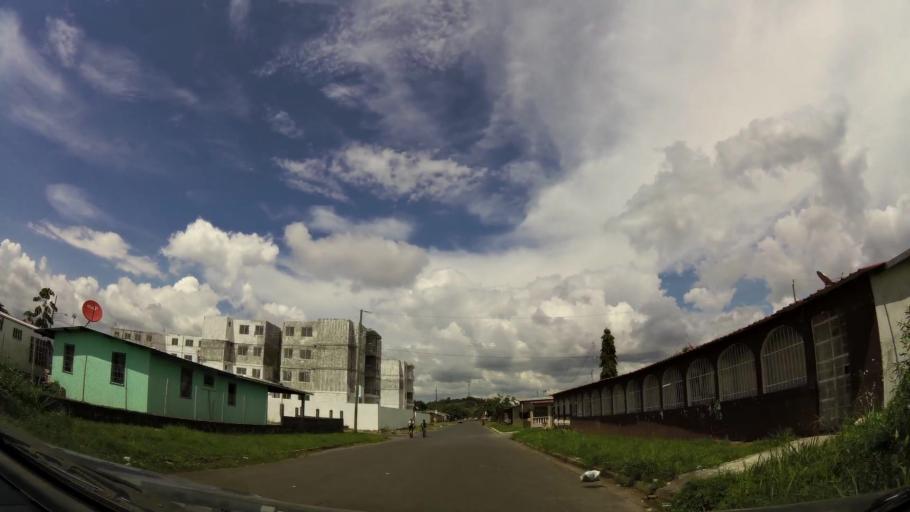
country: PA
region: Panama
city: Nuevo Arraijan
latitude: 8.9100
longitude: -79.7095
